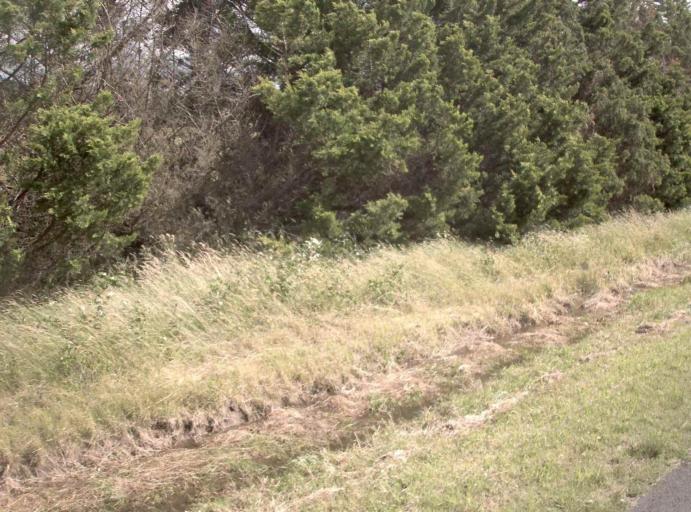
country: AU
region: Victoria
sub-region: Latrobe
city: Morwell
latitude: -38.2948
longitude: 146.4244
